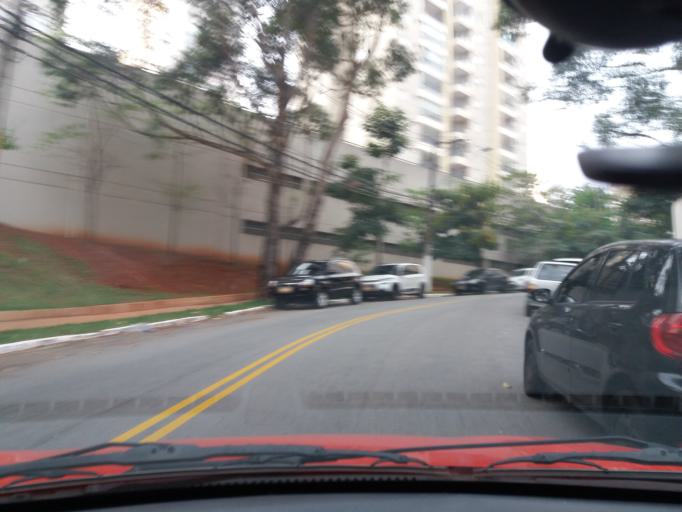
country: BR
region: Sao Paulo
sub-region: Taboao Da Serra
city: Taboao da Serra
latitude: -23.6247
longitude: -46.7426
